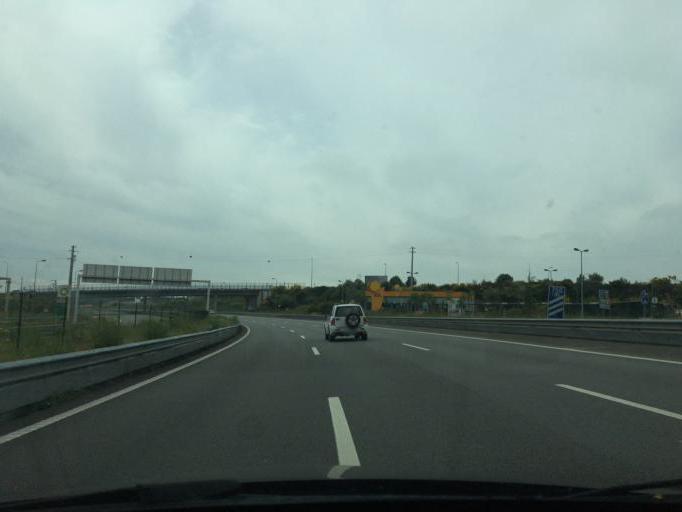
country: PT
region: Porto
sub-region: Maia
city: Gemunde
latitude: 41.2371
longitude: -8.6534
